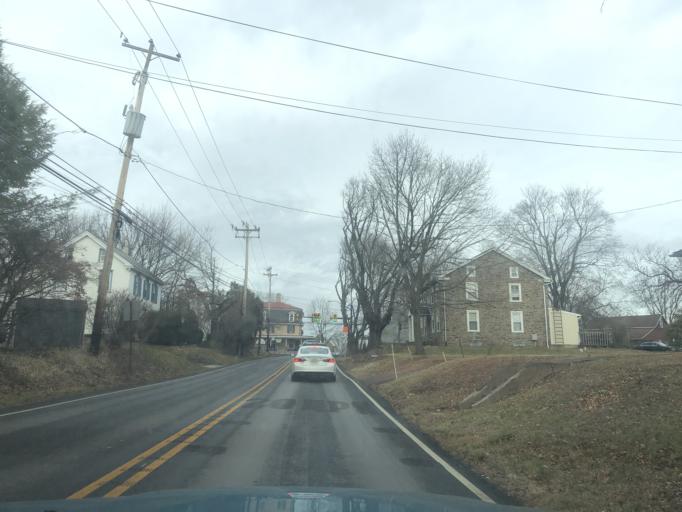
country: US
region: Pennsylvania
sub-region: Montgomery County
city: Harleysville
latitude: 40.2605
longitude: -75.4065
